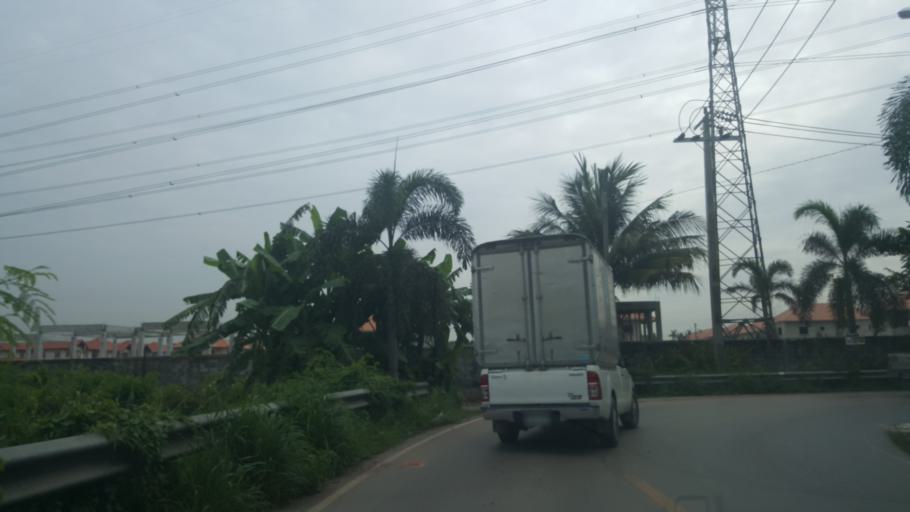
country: TH
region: Bangkok
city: Bang Bon
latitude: 13.6784
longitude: 100.3959
